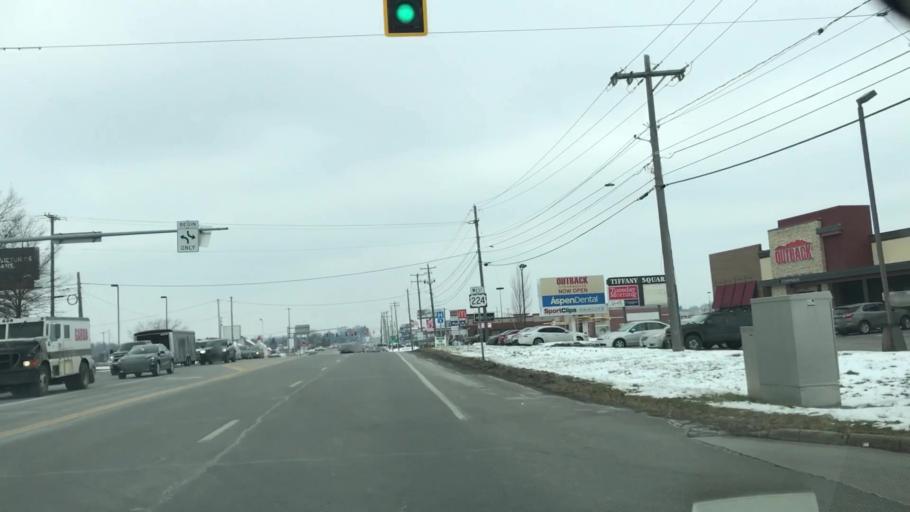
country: US
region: Ohio
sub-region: Mahoning County
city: Poland
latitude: 41.0244
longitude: -80.6302
